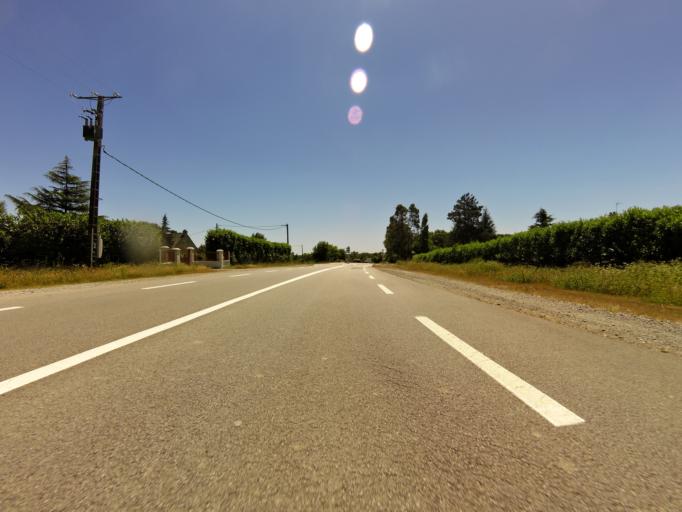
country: FR
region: Brittany
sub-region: Departement du Morbihan
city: Ferel
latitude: 47.5183
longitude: -2.3718
